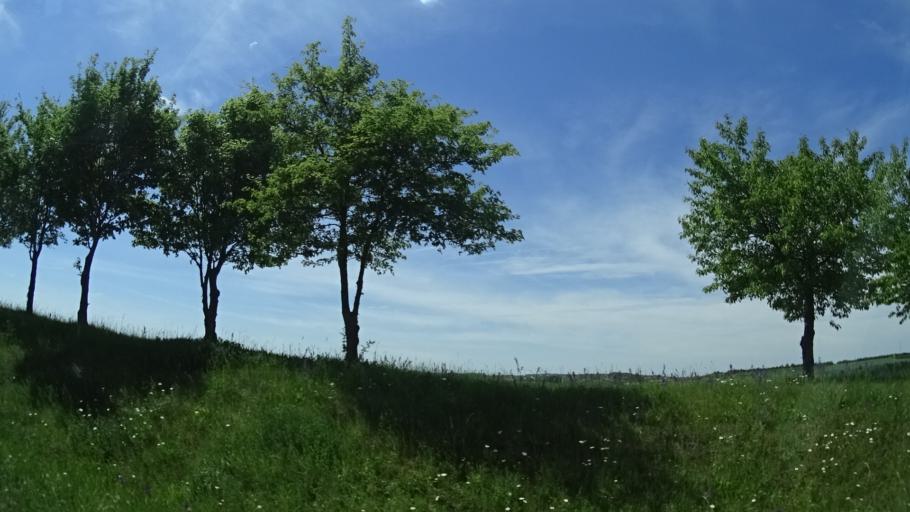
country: DE
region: Bavaria
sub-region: Regierungsbezirk Unterfranken
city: Oerlenbach
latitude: 50.1568
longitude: 10.1487
